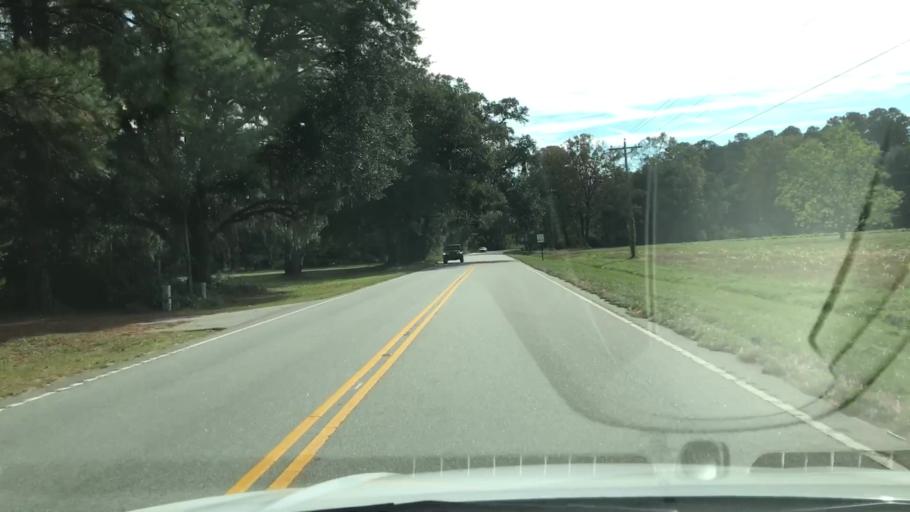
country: US
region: South Carolina
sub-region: Charleston County
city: Ravenel
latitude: 32.7815
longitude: -80.4681
